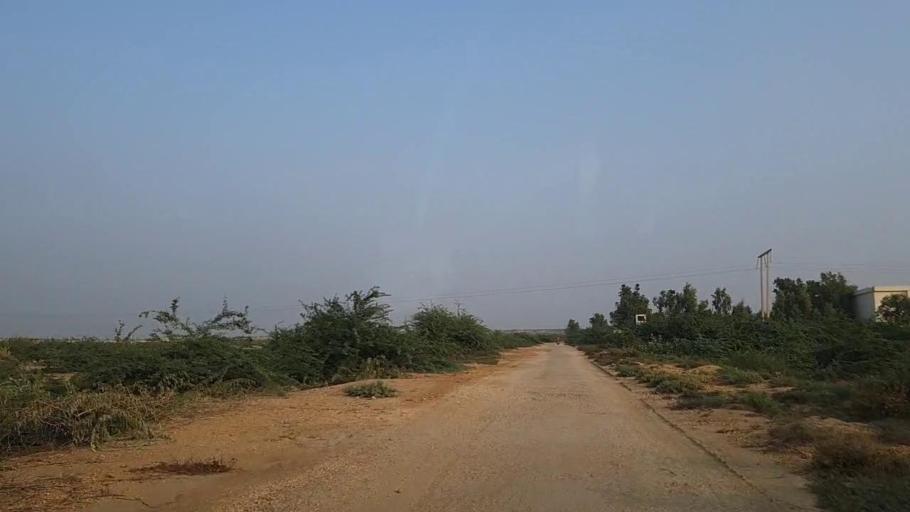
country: PK
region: Sindh
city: Thatta
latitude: 24.6908
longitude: 67.8456
